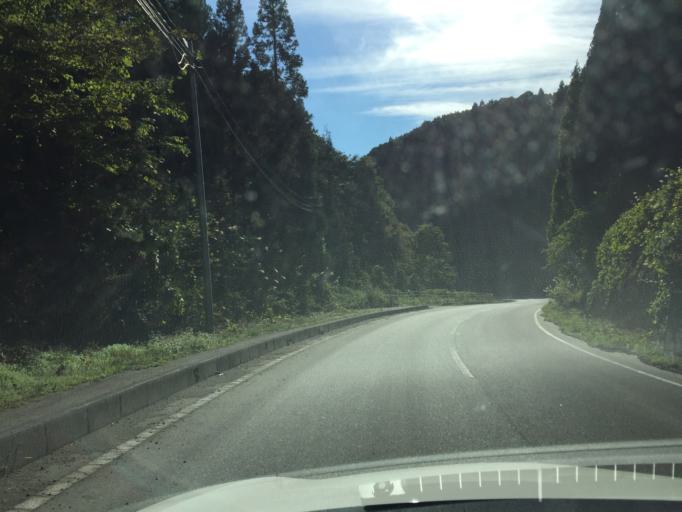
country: JP
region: Fukushima
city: Ishikawa
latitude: 37.1304
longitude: 140.5913
